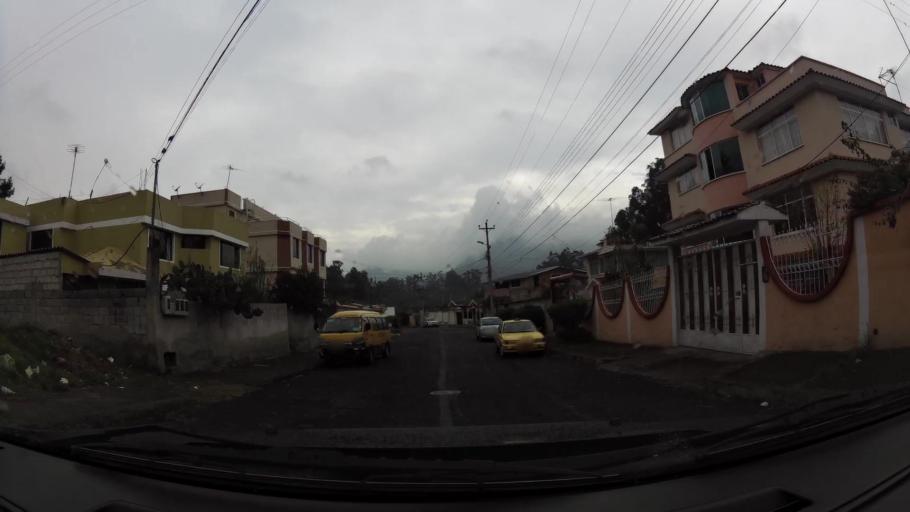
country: EC
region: Pichincha
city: Sangolqui
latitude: -0.2883
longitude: -78.4621
